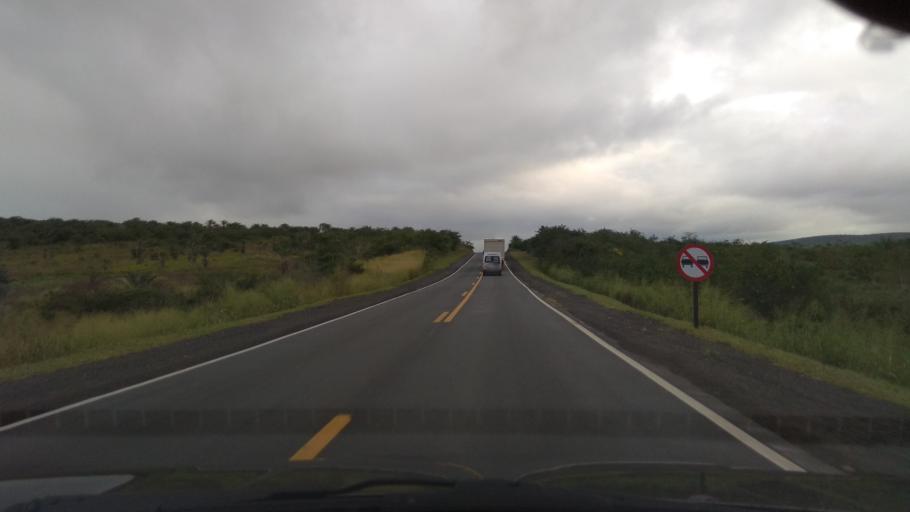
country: BR
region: Bahia
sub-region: Jaguaquara
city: Jaguaquara
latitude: -13.3874
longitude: -40.0217
